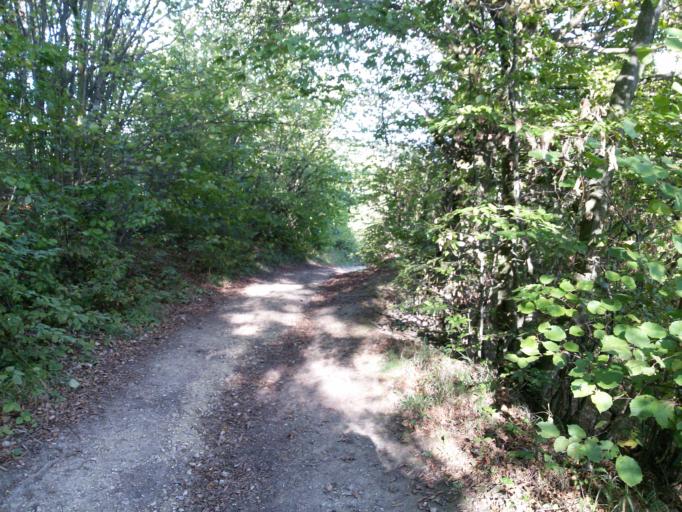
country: CZ
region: South Moravian
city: Boritov
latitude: 49.4506
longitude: 16.5877
